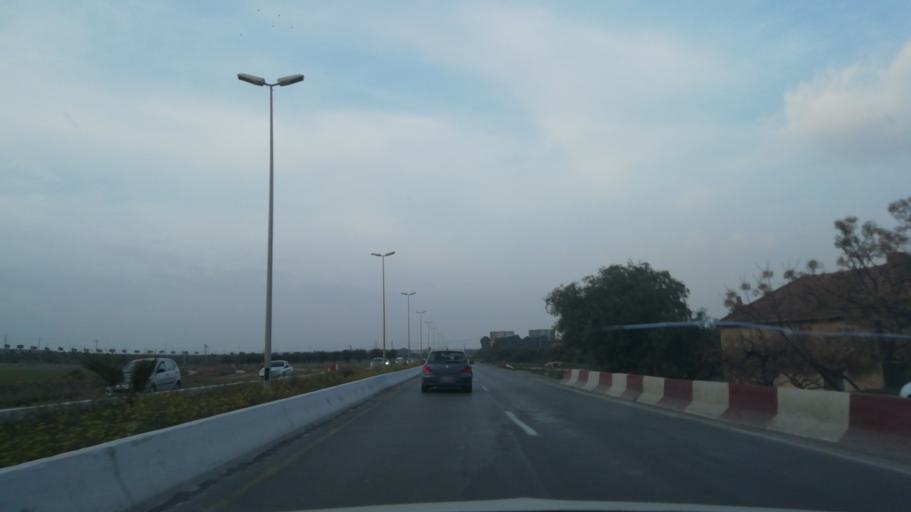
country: DZ
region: Sidi Bel Abbes
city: Sidi Bel Abbes
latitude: 35.1985
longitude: -0.6609
